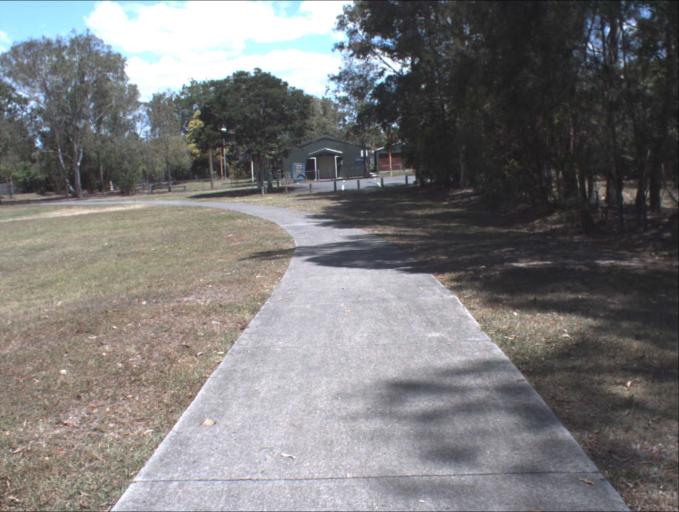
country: AU
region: Queensland
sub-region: Logan
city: Rochedale South
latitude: -27.6013
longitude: 153.1148
